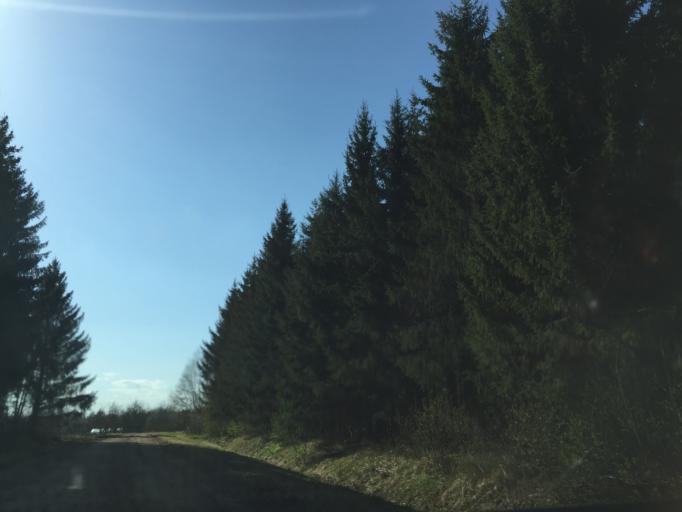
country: LV
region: Kegums
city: Kegums
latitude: 56.8794
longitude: 24.7933
